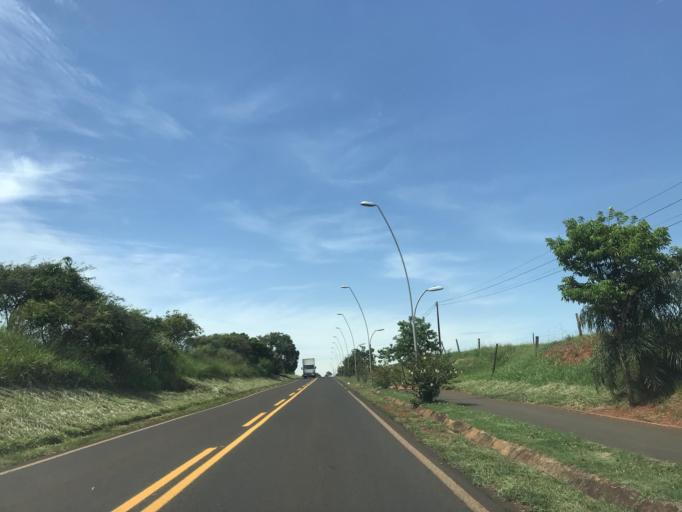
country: BR
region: Parana
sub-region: Terra Rica
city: Terra Rica
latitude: -22.7465
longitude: -52.6251
